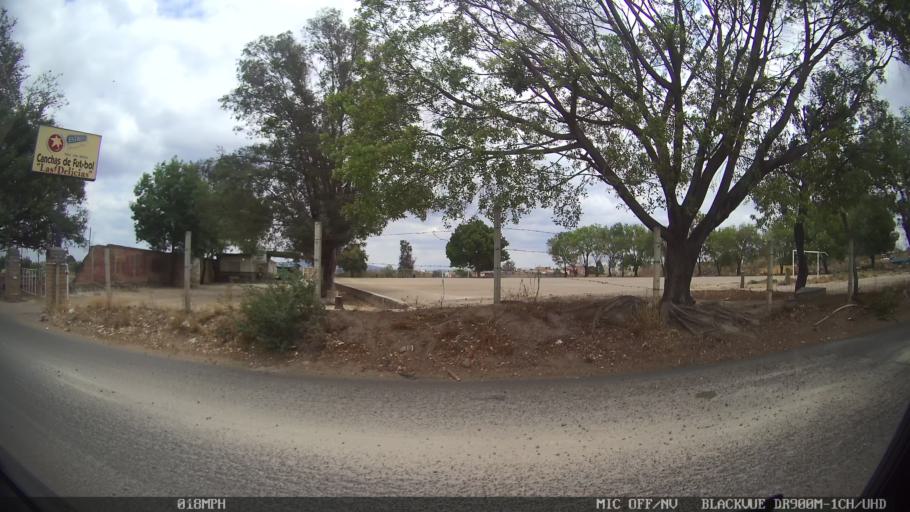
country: MX
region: Jalisco
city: Tonala
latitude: 20.6405
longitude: -103.2573
